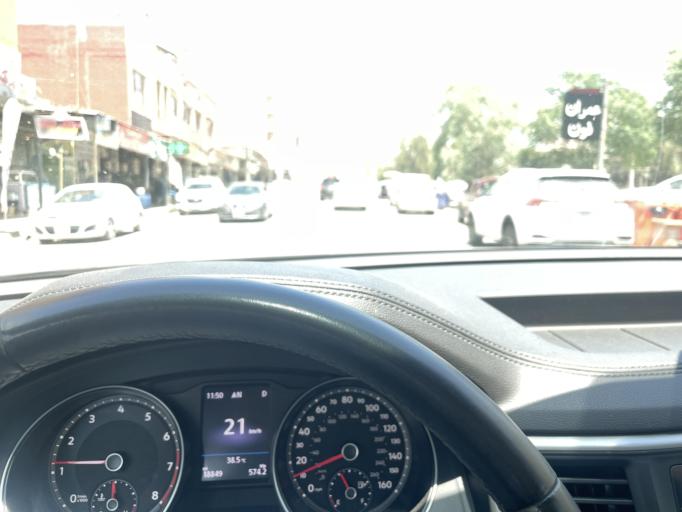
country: IQ
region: Dahuk
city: Saymayl
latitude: 36.8580
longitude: 42.9053
